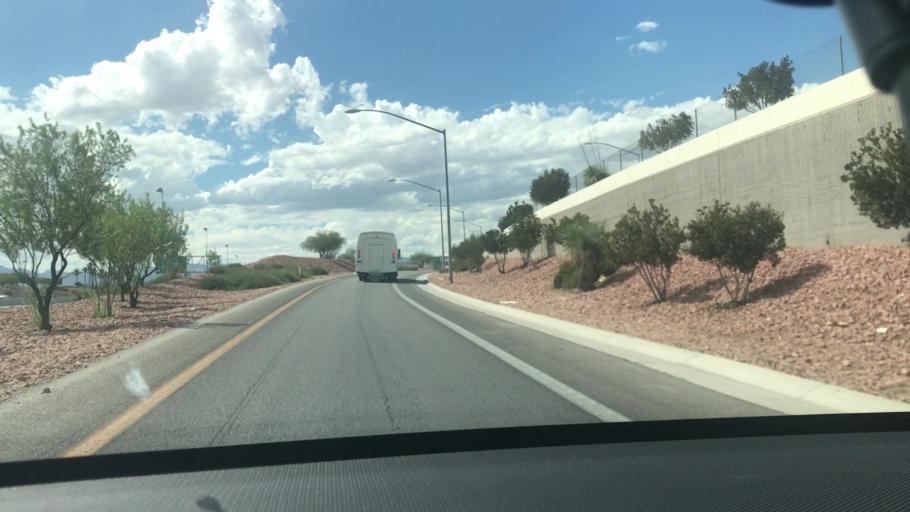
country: US
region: Nevada
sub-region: Clark County
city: Paradise
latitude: 36.0640
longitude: -115.1668
